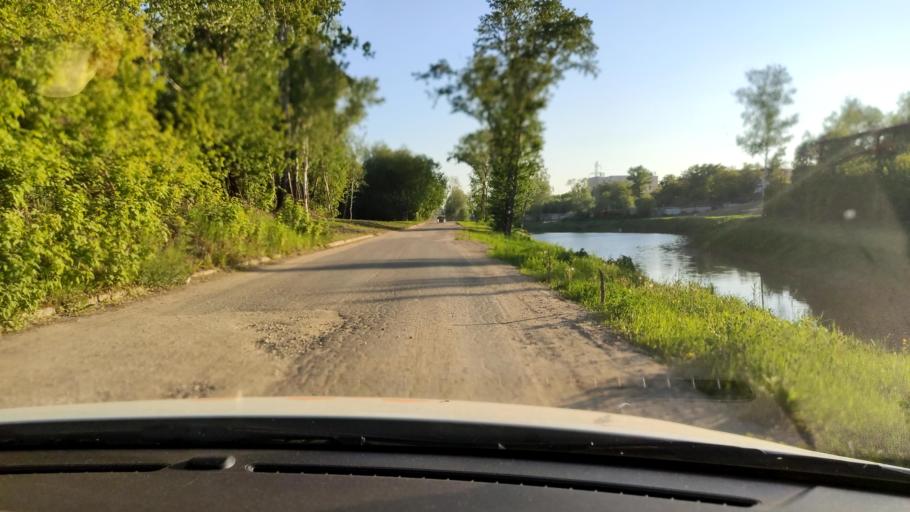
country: RU
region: Tatarstan
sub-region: Gorod Kazan'
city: Kazan
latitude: 55.8022
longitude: 49.0498
